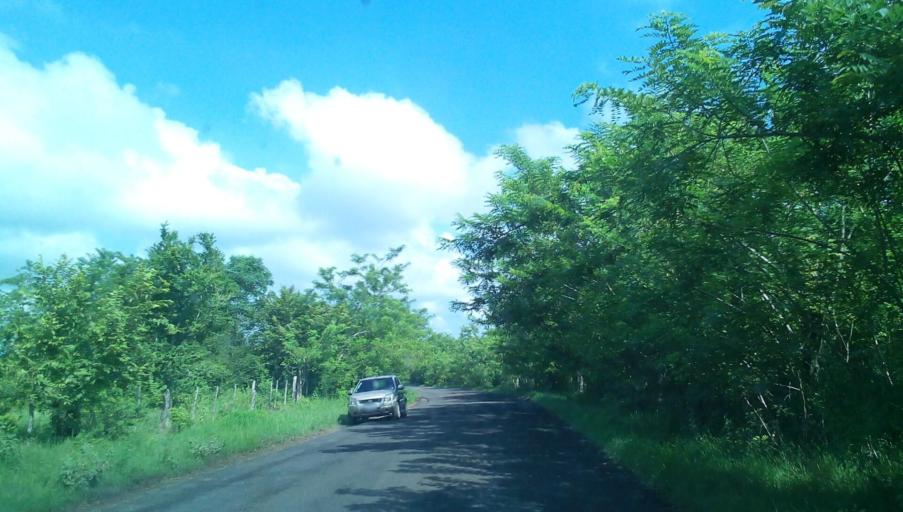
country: MX
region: Veracruz
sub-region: Citlaltepetl
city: Las Sabinas
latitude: 21.3452
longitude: -97.8910
